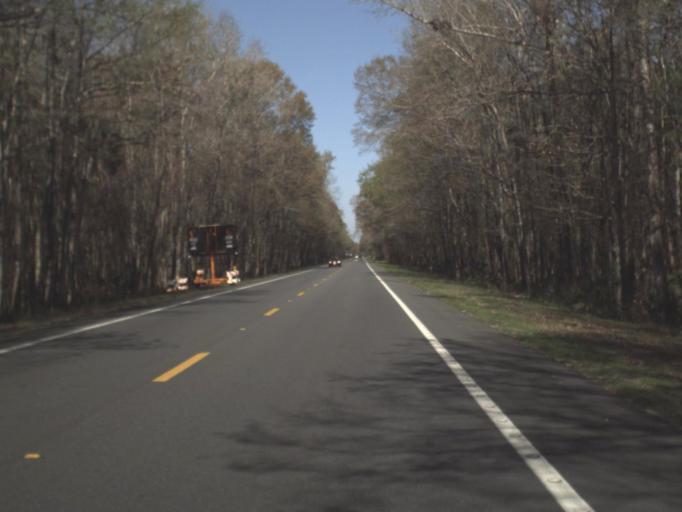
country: US
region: Florida
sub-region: Leon County
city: Woodville
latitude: 30.1516
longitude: -83.9846
